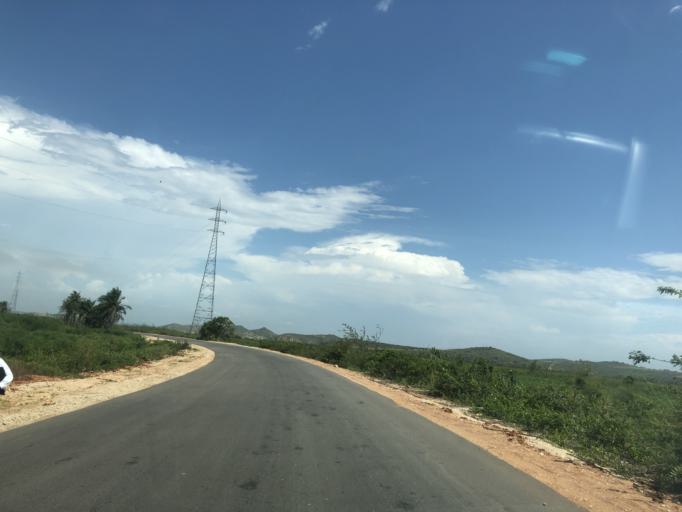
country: AO
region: Cuanza Sul
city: Sumbe
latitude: -10.8805
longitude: 13.8402
